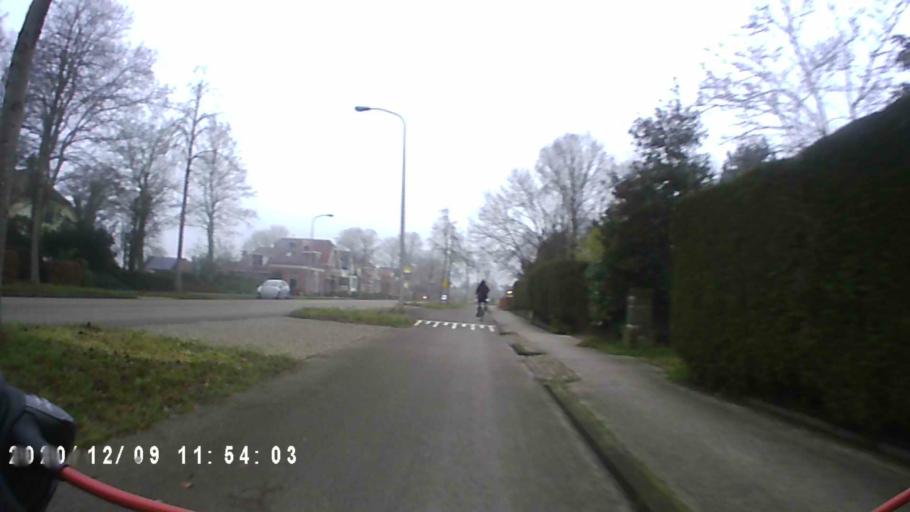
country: NL
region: Groningen
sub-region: Gemeente Haren
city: Haren
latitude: 53.1813
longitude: 6.5933
